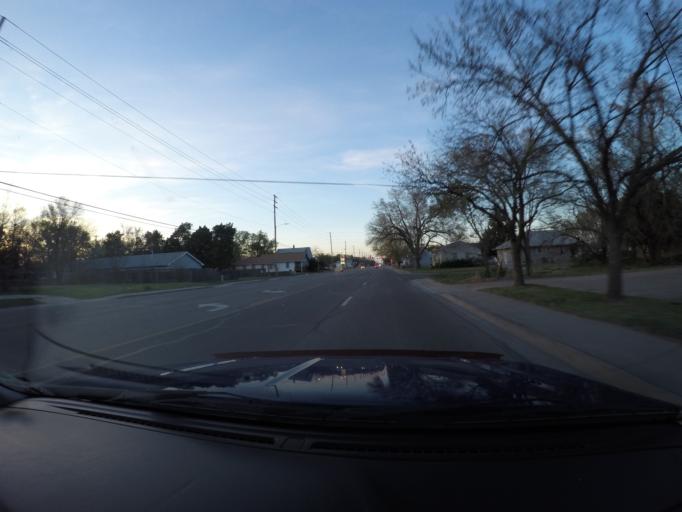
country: US
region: Kansas
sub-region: Saline County
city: Salina
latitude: 38.8389
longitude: -97.5939
